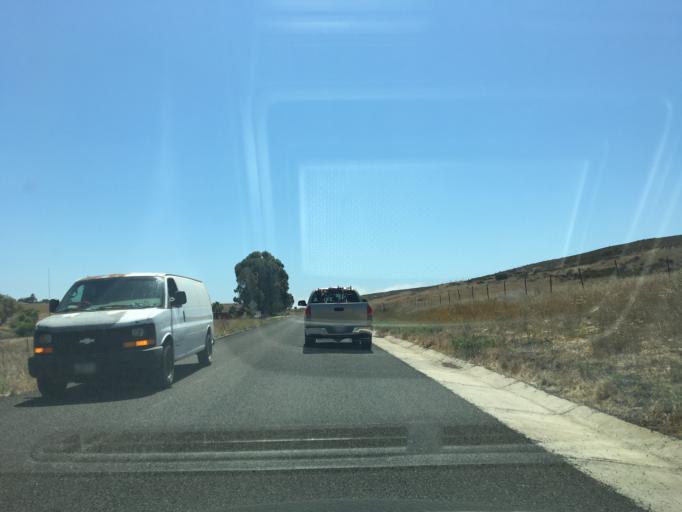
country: MX
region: Baja California
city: El Sauzal
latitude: 31.9926
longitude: -116.7057
